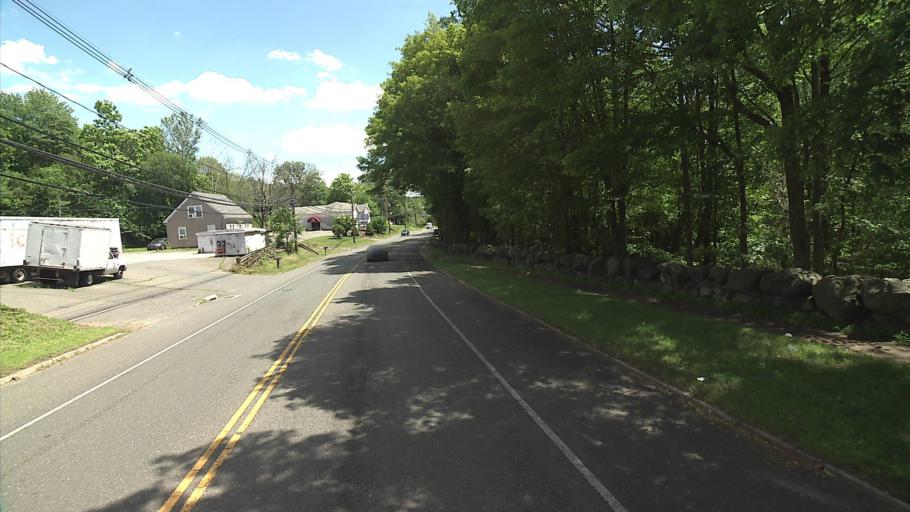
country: US
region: Connecticut
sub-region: New Haven County
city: Naugatuck
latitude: 41.4774
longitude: -73.0464
